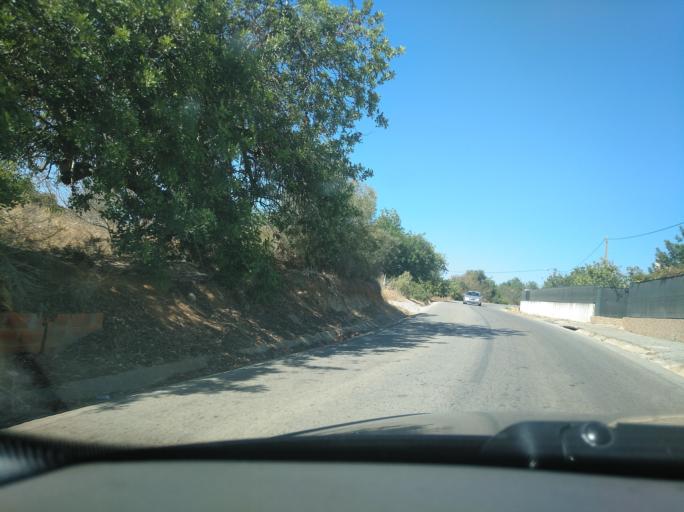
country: PT
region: Faro
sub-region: Faro
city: Faro
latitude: 37.0548
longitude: -7.9016
